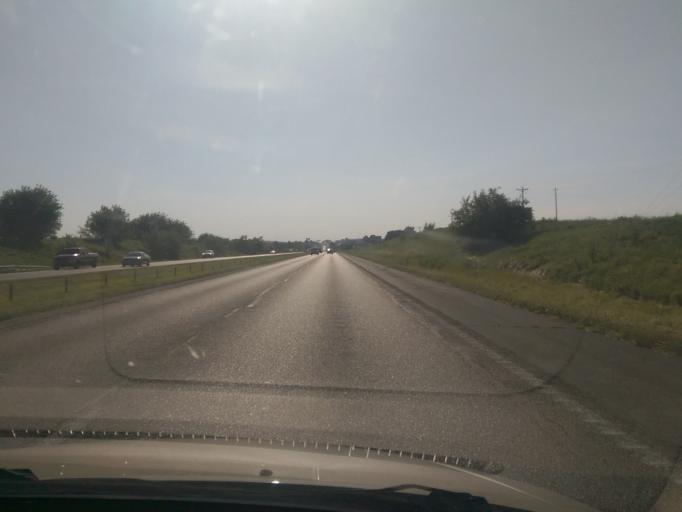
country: US
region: Missouri
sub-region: Lafayette County
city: Odessa
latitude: 39.0062
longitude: -93.9001
